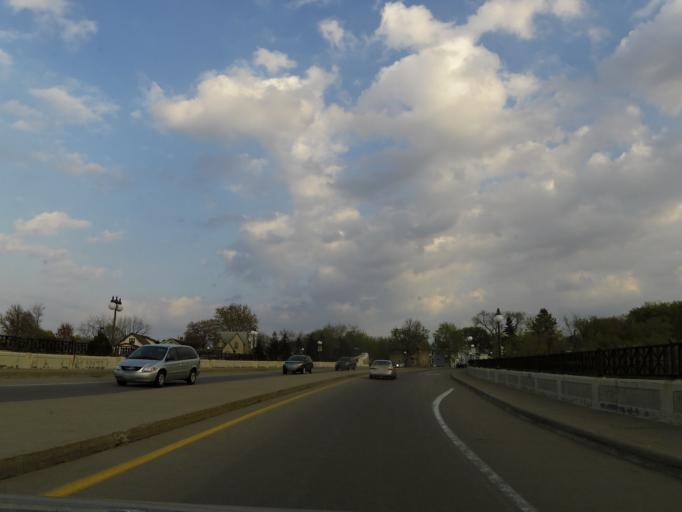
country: US
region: Minnesota
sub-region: Dakota County
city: West Saint Paul
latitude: 44.9317
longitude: -93.1025
